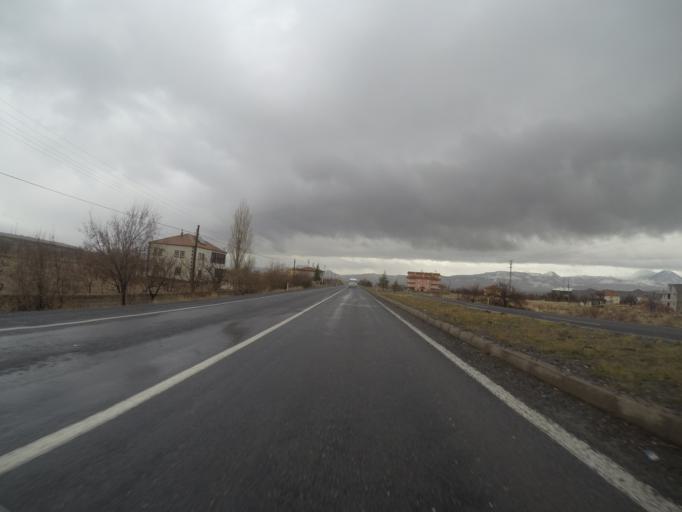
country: TR
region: Kayseri
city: Incesu
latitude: 38.6810
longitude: 35.2185
